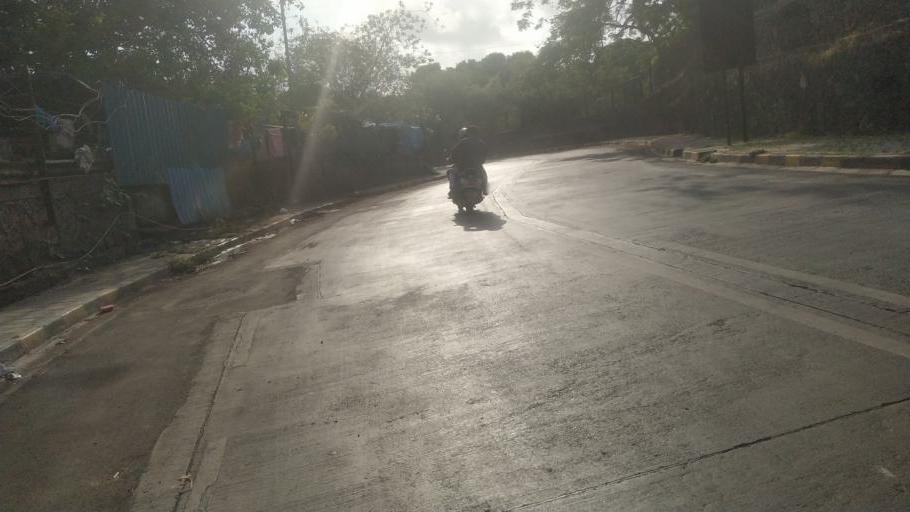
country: IN
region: Maharashtra
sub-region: Mumbai Suburban
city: Mumbai
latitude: 19.0191
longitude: 72.8596
